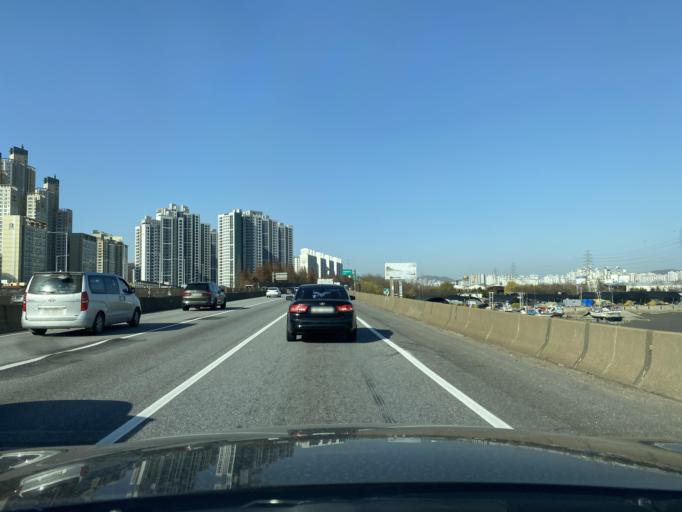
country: KR
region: Incheon
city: Incheon
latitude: 37.3985
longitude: 126.7421
